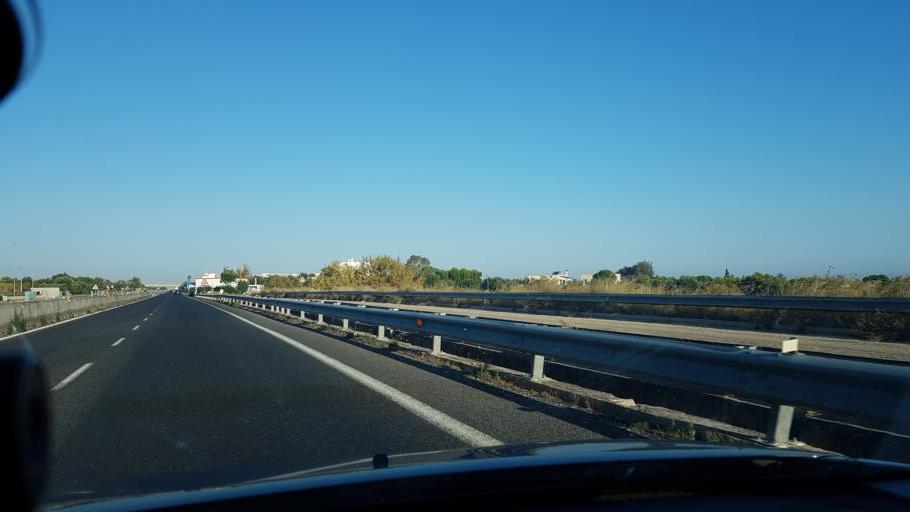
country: IT
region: Apulia
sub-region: Provincia di Bari
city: Monopoli
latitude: 40.9261
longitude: 17.3107
